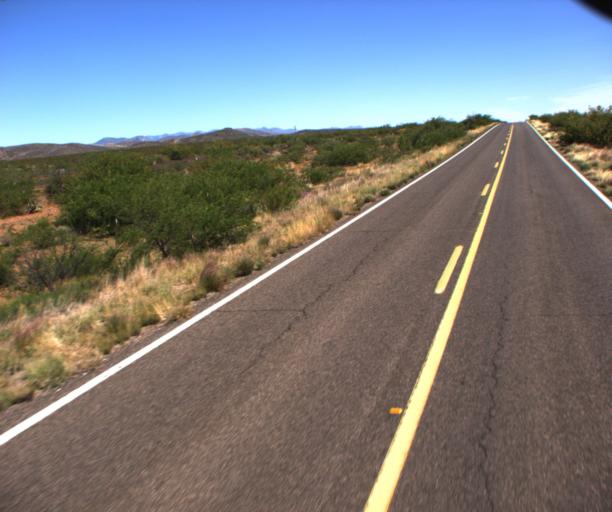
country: US
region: Arizona
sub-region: Cochise County
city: Douglas
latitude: 31.4828
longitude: -109.3474
